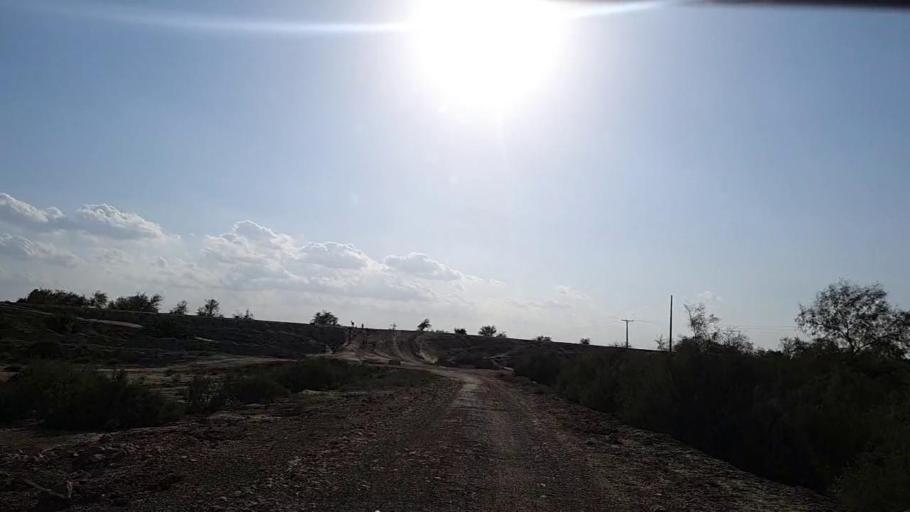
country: PK
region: Sindh
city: Johi
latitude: 26.5859
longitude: 67.5423
